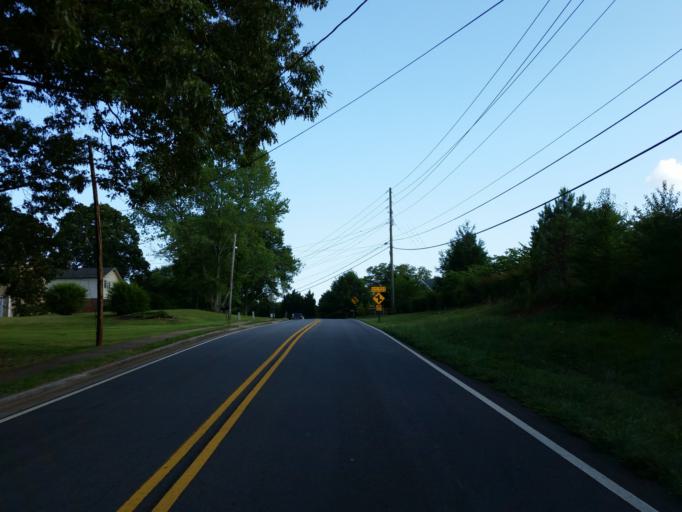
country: US
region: Georgia
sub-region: Cherokee County
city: Woodstock
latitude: 34.0487
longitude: -84.4849
